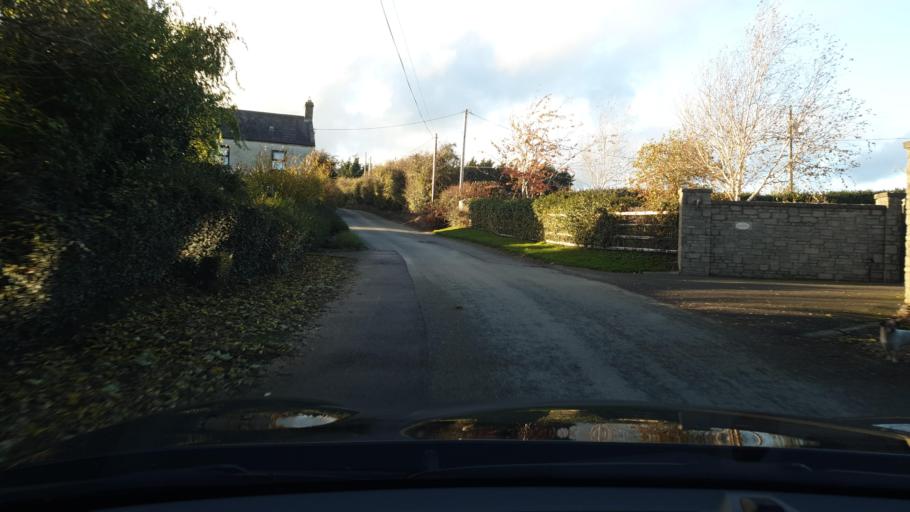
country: IE
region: Leinster
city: Balrothery
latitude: 53.5901
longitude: -6.1983
